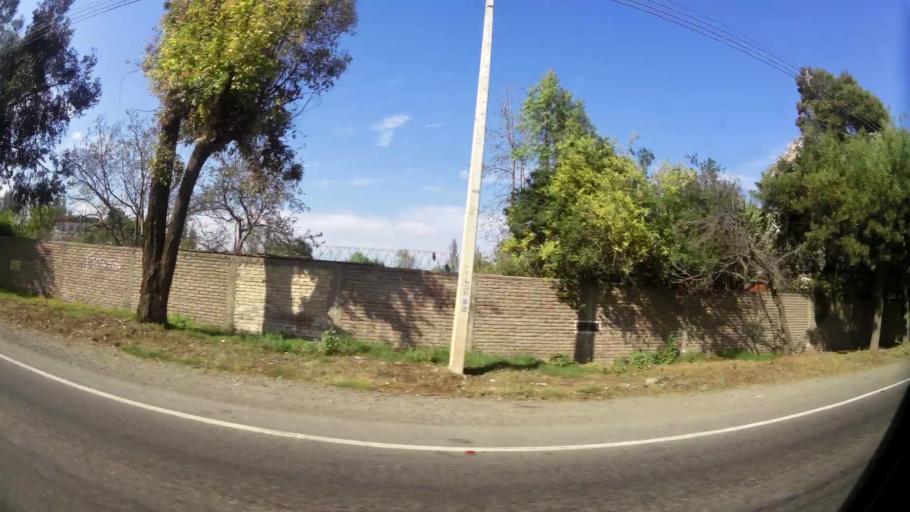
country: CL
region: Santiago Metropolitan
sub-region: Provincia de Talagante
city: Penaflor
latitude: -33.5527
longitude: -70.8364
